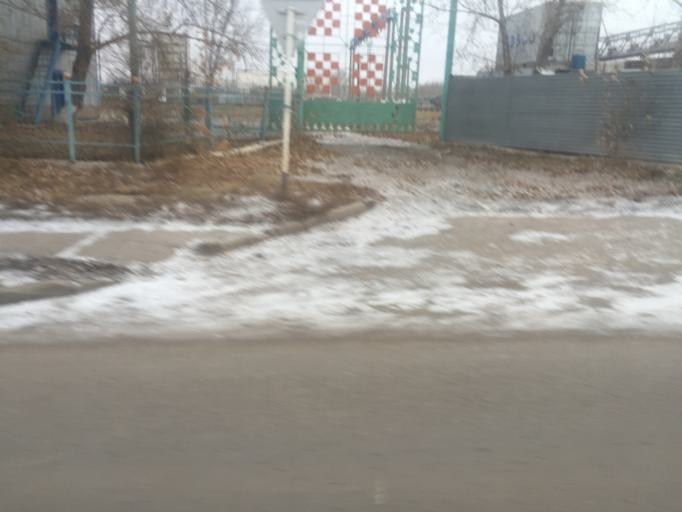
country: KZ
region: Astana Qalasy
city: Astana
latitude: 51.2029
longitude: 71.3850
